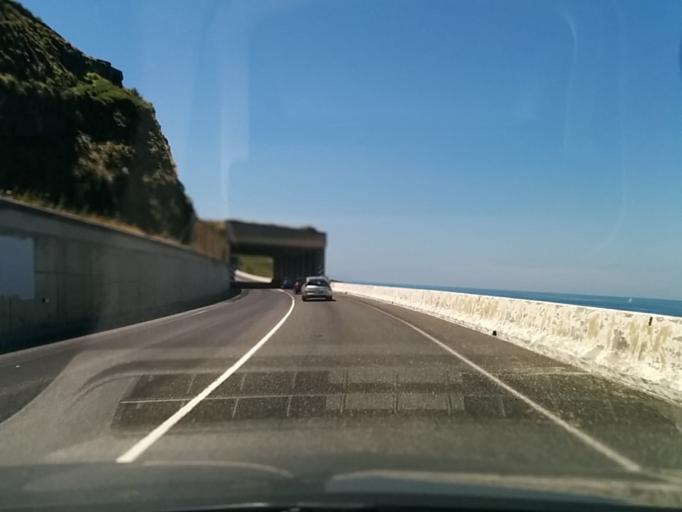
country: ES
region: Basque Country
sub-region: Provincia de Guipuzcoa
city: Getaria
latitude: 43.3086
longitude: -2.2166
